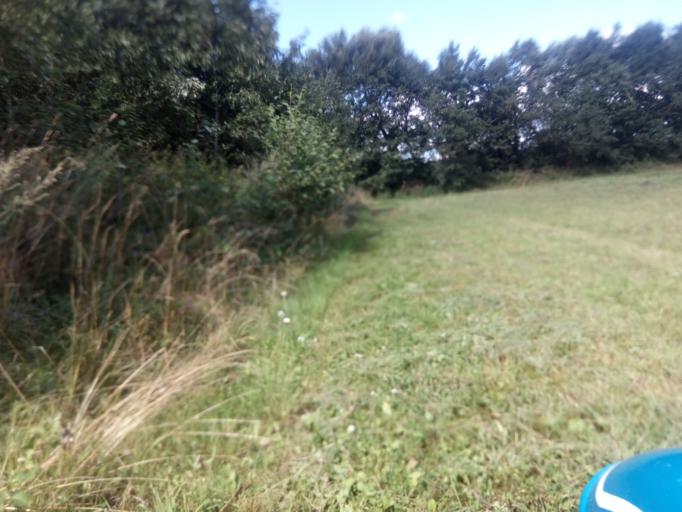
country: BY
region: Vitebsk
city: Dzisna
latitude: 55.6785
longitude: 28.3191
